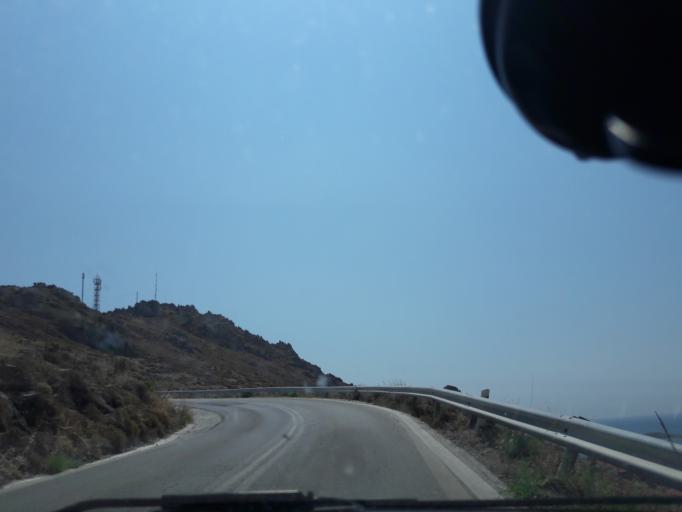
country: GR
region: North Aegean
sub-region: Nomos Lesvou
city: Myrina
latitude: 39.8625
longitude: 25.0785
